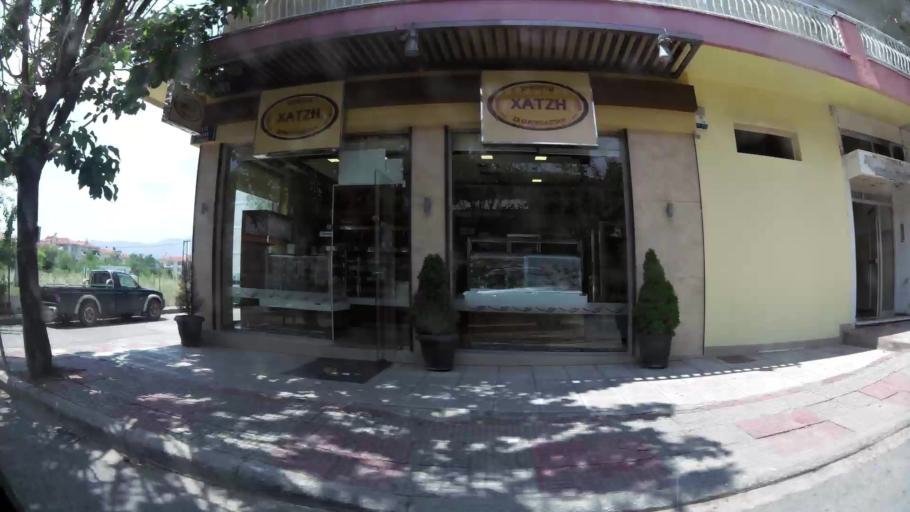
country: GR
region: West Macedonia
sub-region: Nomos Kozanis
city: Kozani
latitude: 40.2948
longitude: 21.7982
